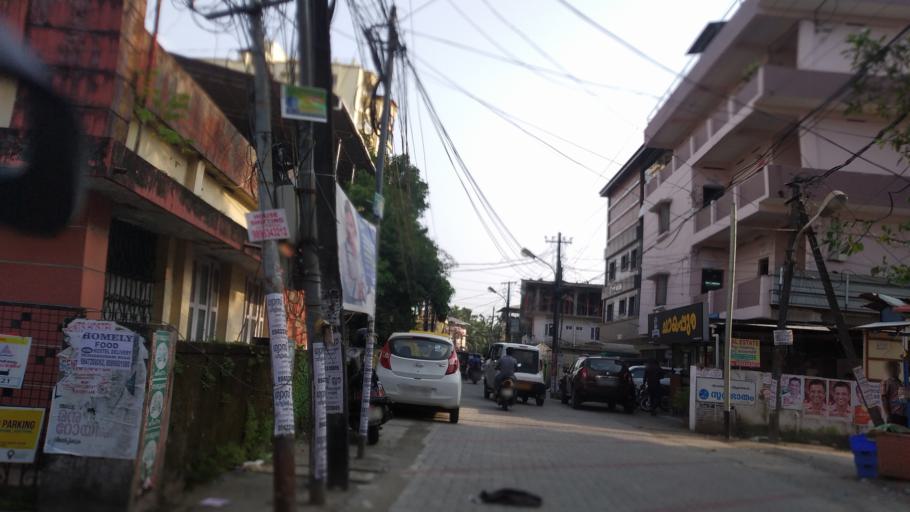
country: IN
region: Kerala
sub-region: Ernakulam
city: Cochin
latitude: 9.9877
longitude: 76.2890
